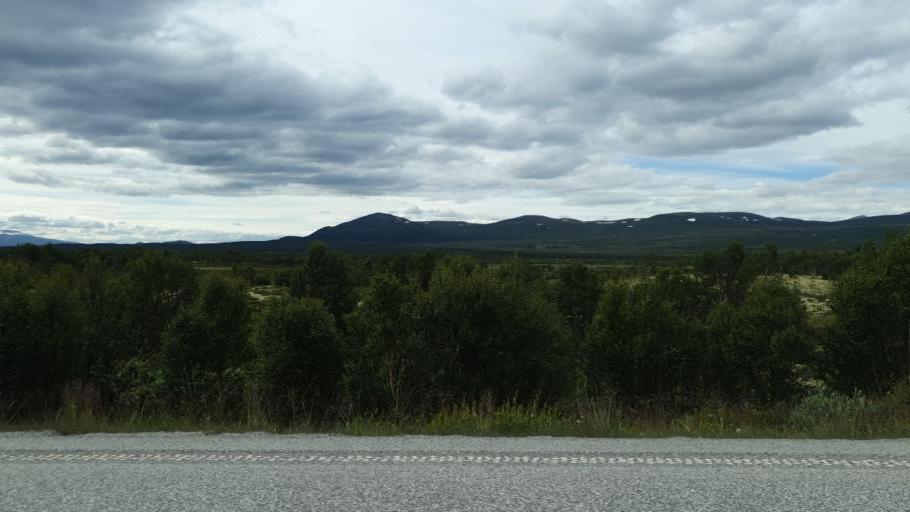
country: NO
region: Oppland
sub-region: Dovre
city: Dovre
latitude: 62.1261
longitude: 9.3058
